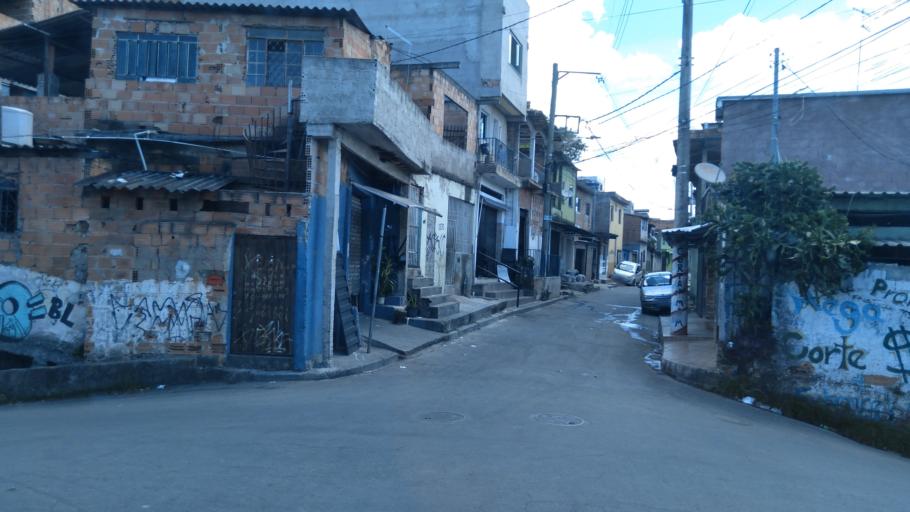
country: BR
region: Minas Gerais
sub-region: Belo Horizonte
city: Belo Horizonte
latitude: -19.8439
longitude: -43.8980
